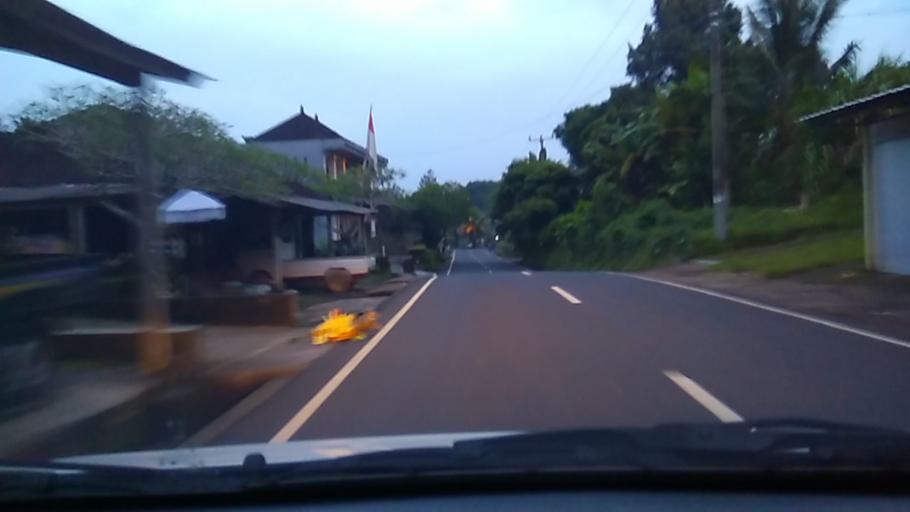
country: ID
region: Bali
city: Kekeran
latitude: -8.4729
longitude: 115.1904
